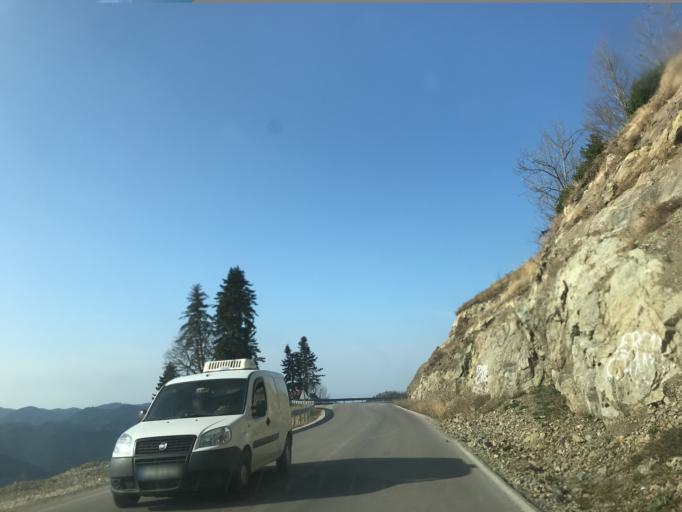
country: TR
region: Bolu
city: Bolu
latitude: 40.8839
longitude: 31.6829
